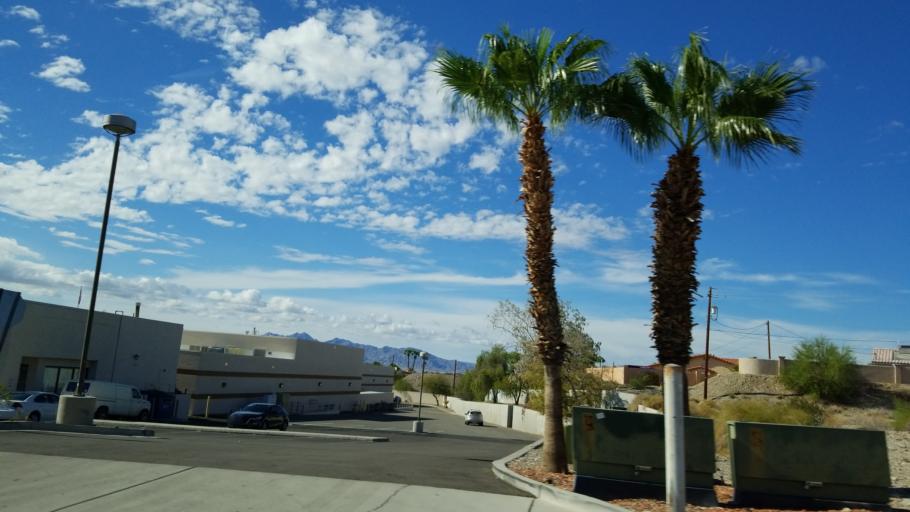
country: US
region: Arizona
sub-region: Mohave County
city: Lake Havasu City
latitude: 34.4769
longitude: -114.3209
